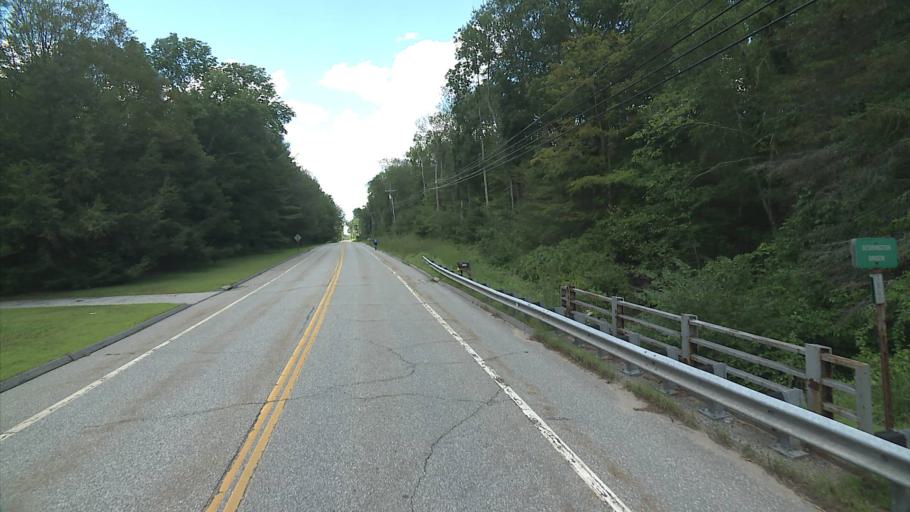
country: US
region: Connecticut
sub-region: Tolland County
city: Storrs
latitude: 41.8466
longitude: -72.1638
